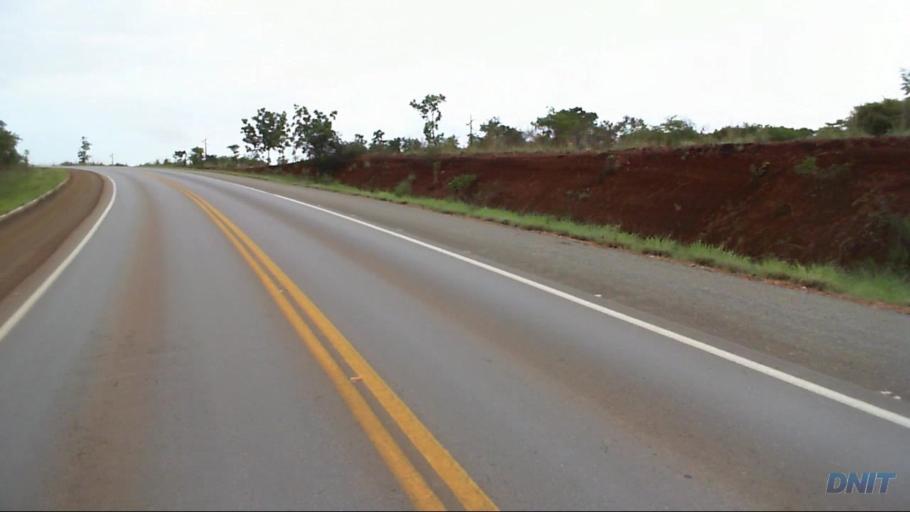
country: BR
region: Goias
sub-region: Uruacu
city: Uruacu
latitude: -14.7426
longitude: -49.0806
